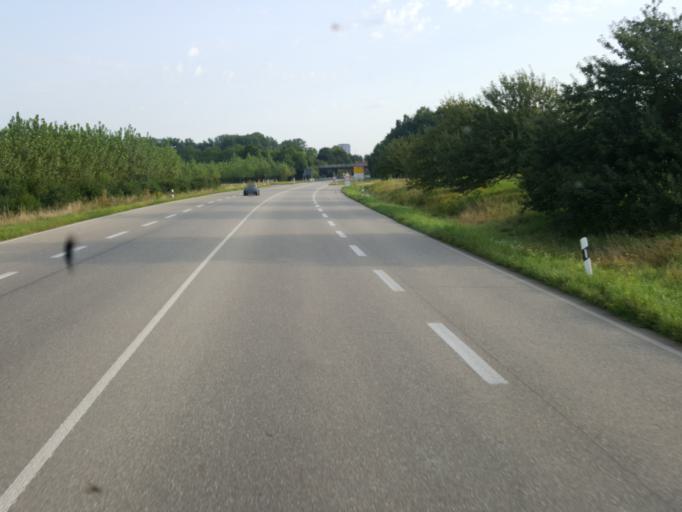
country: DE
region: Baden-Wuerttemberg
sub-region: Freiburg Region
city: Kippenheim
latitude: 48.3234
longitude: 7.8357
